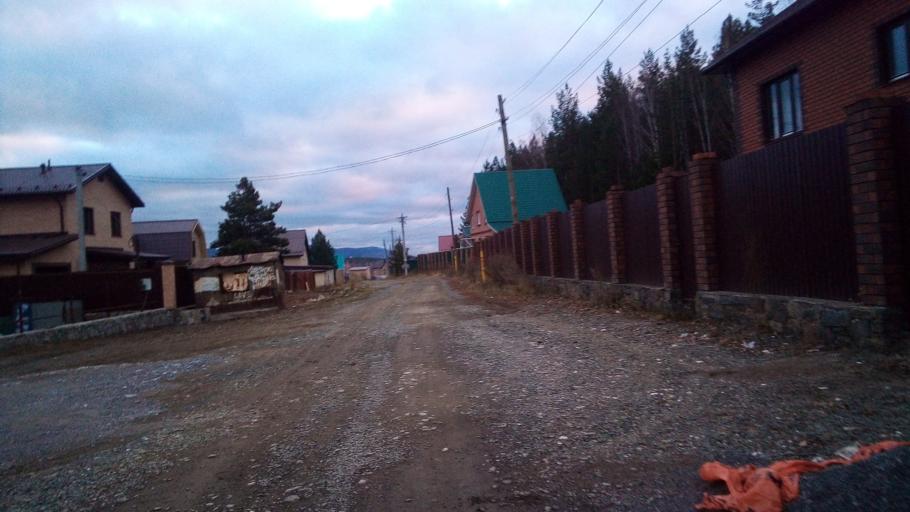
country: RU
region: Chelyabinsk
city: Turgoyak
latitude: 55.1771
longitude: 60.1312
